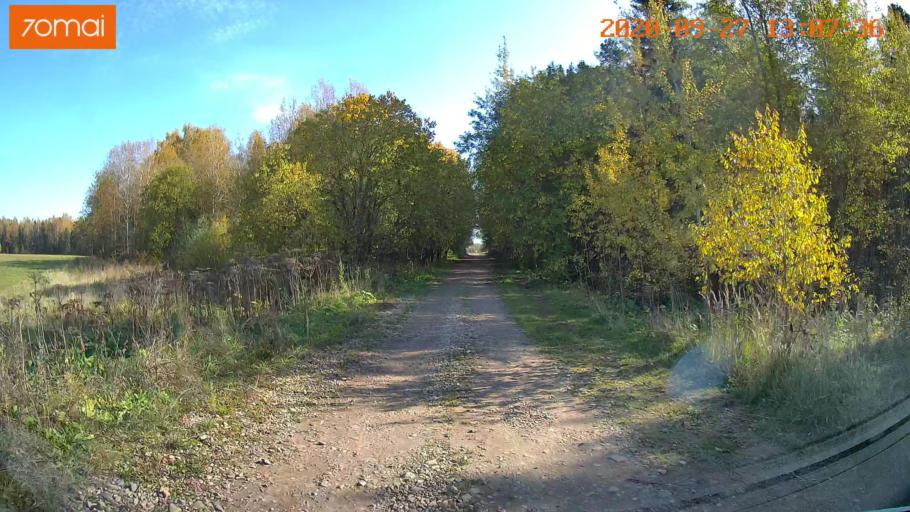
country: RU
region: Ivanovo
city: Furmanov
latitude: 57.1636
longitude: 41.0760
